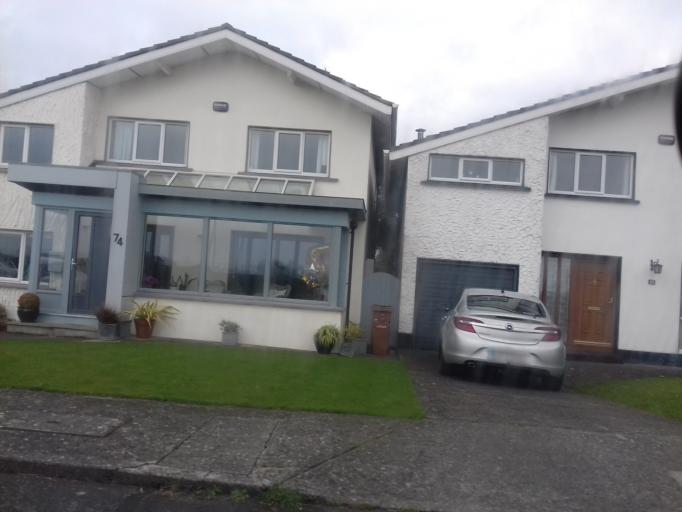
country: IE
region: Leinster
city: Portmarnock
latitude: 53.4225
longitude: -6.1311
